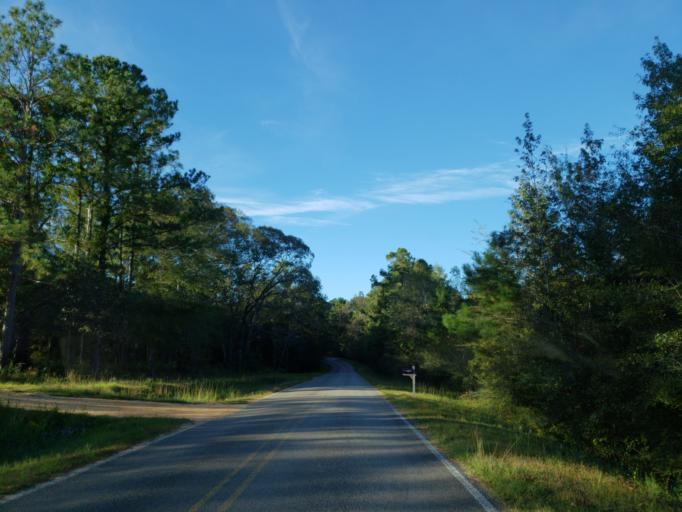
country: US
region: Mississippi
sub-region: Perry County
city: Richton
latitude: 31.3438
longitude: -88.8083
